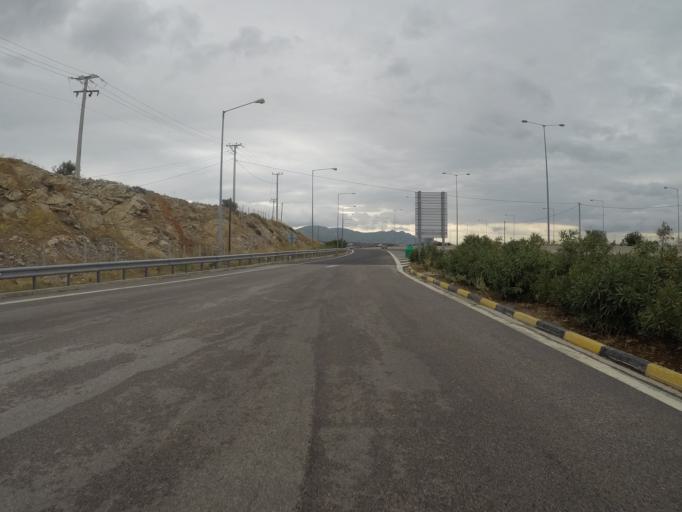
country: GR
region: Attica
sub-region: Nomarchia Dytikis Attikis
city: Megara
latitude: 37.9970
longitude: 23.3680
